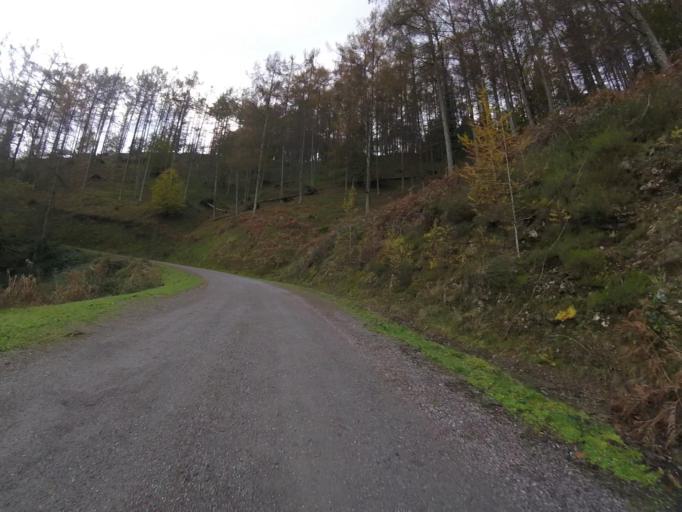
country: ES
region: Navarre
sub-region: Provincia de Navarra
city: Goizueta
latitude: 43.2174
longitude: -1.8225
